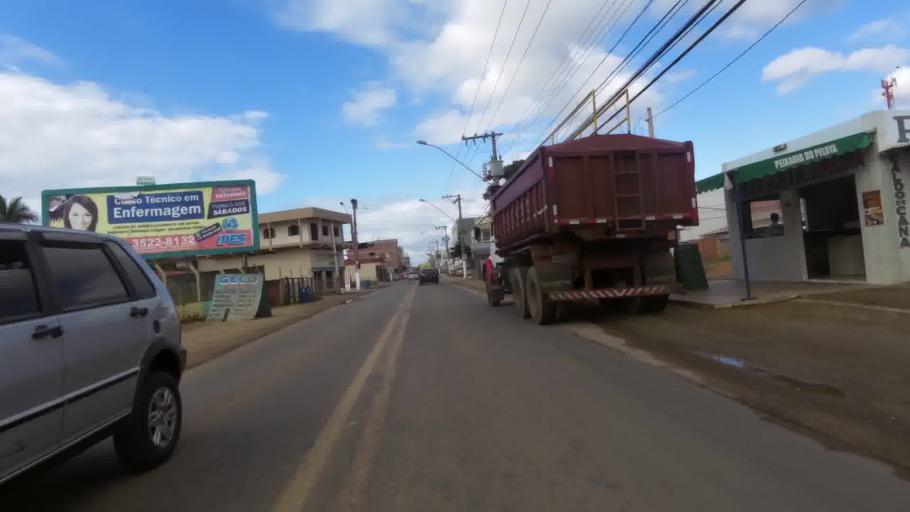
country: BR
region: Espirito Santo
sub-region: Piuma
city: Piuma
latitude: -20.8935
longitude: -40.7758
